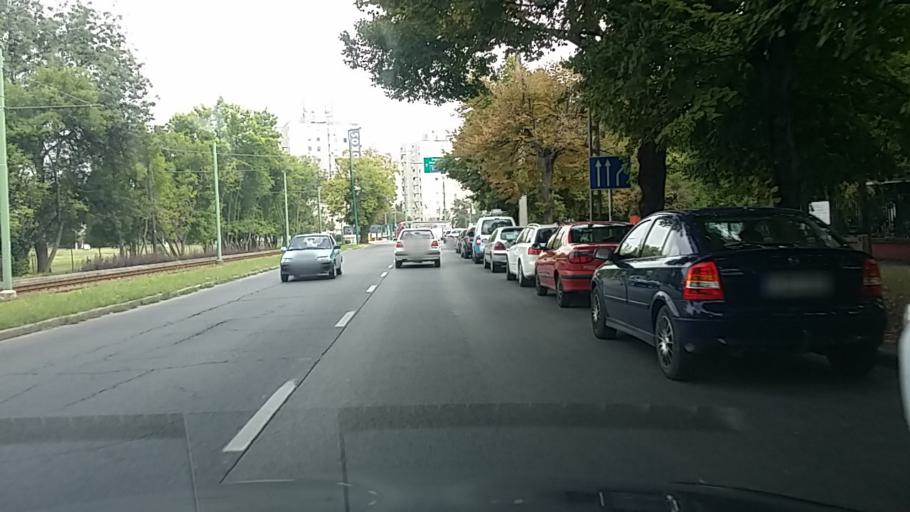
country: HU
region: Csongrad
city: Szeged
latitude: 46.2710
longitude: 20.1585
